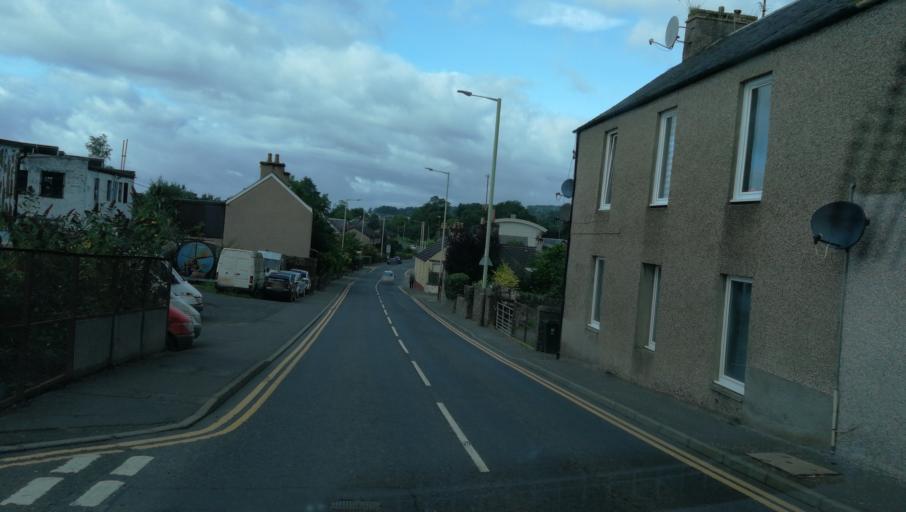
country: GB
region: Scotland
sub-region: Perth and Kinross
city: Blairgowrie
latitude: 56.5962
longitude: -3.3229
